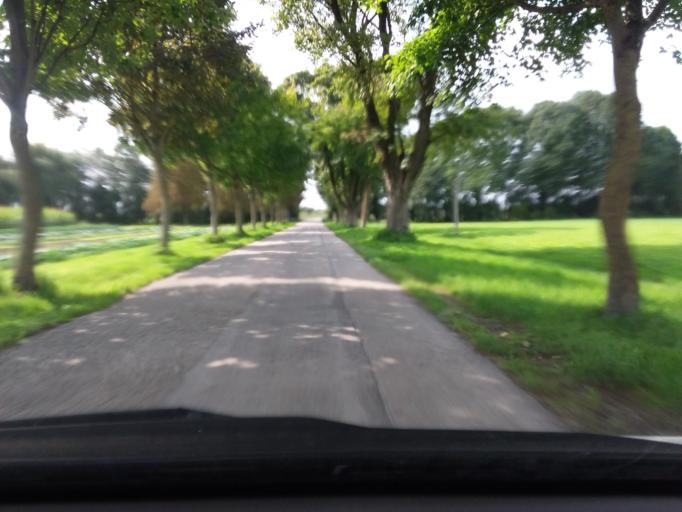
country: DE
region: Bavaria
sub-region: Upper Bavaria
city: Ismaning
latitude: 48.2302
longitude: 11.7248
